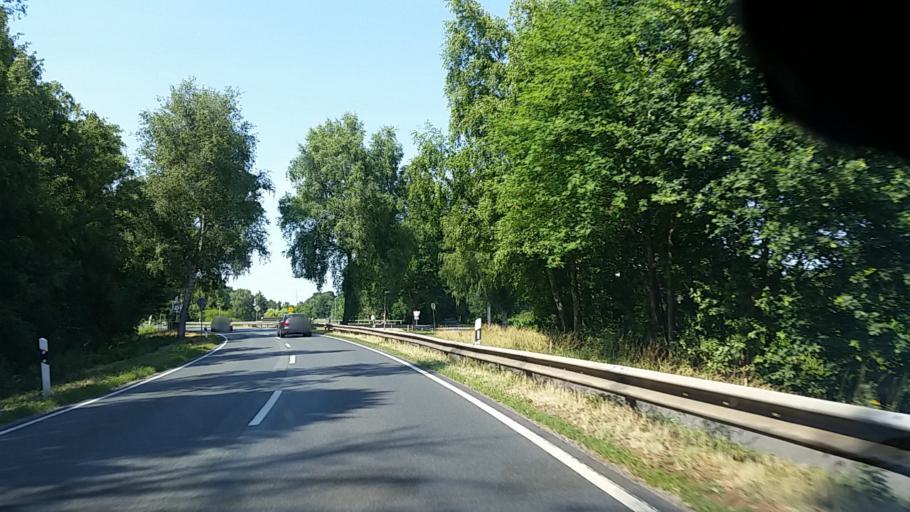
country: DE
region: Lower Saxony
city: Ottersberg
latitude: 53.0656
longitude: 9.1715
